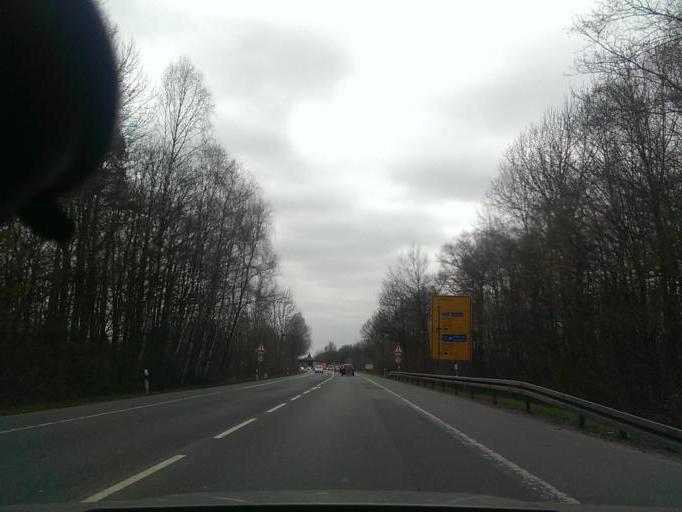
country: DE
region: North Rhine-Westphalia
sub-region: Regierungsbezirk Detmold
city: Rheda-Wiedenbruck
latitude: 51.8337
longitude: 8.3445
